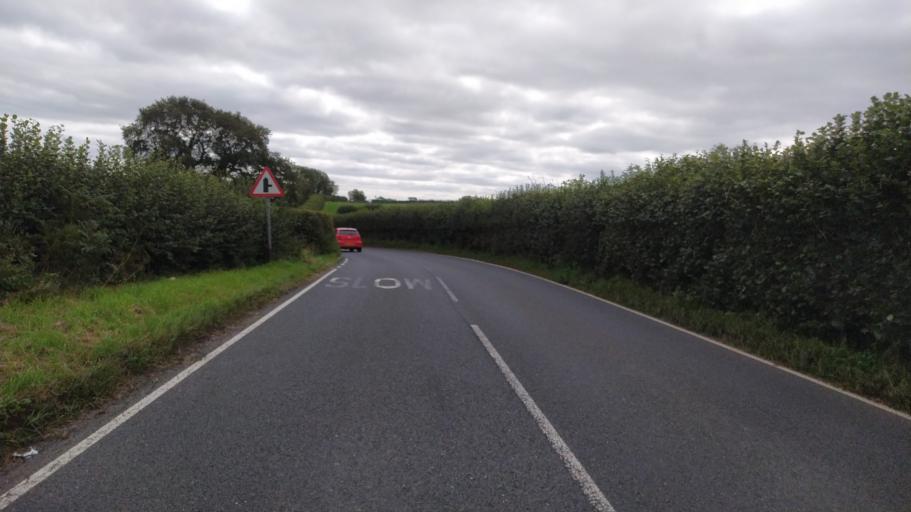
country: GB
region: England
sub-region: Somerset
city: Wincanton
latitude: 51.0607
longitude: -2.3488
